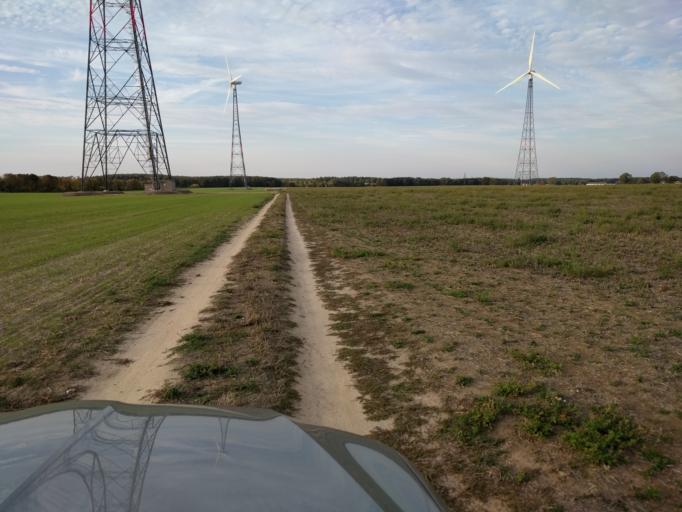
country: DE
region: Brandenburg
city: Ziesar
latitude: 52.2004
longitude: 12.2820
